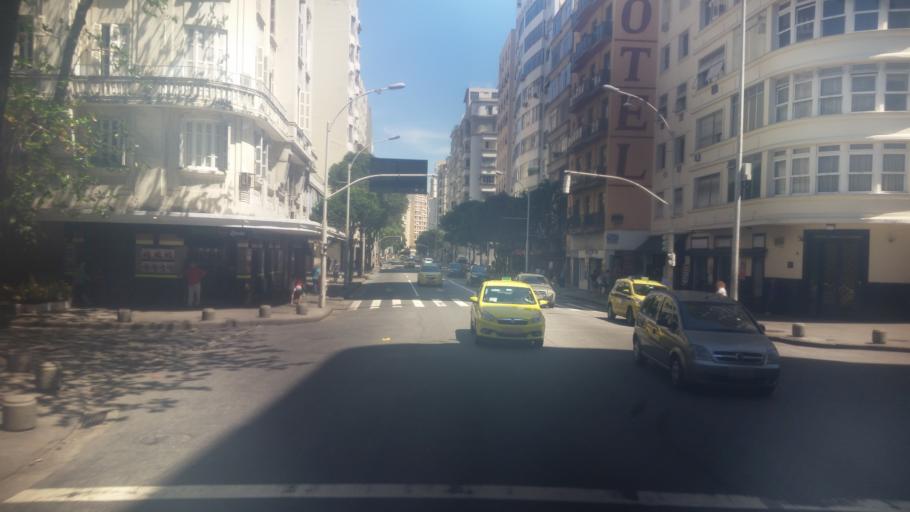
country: BR
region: Rio de Janeiro
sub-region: Rio De Janeiro
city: Rio de Janeiro
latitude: -22.9650
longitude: -43.1769
